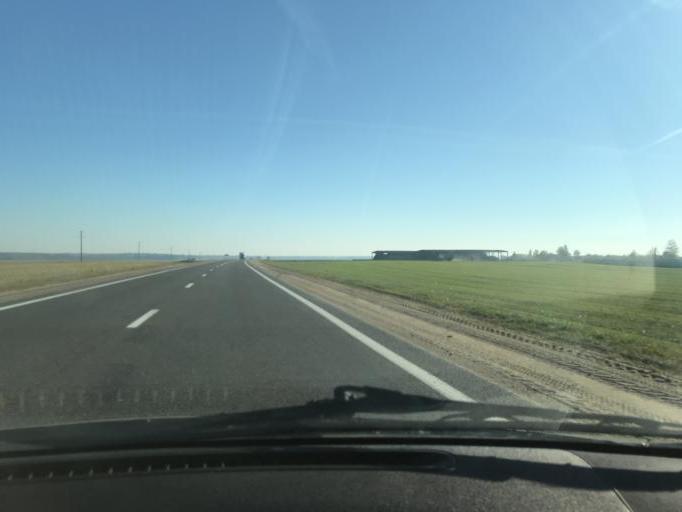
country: BY
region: Brest
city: Ivanava
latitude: 52.1560
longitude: 25.6391
